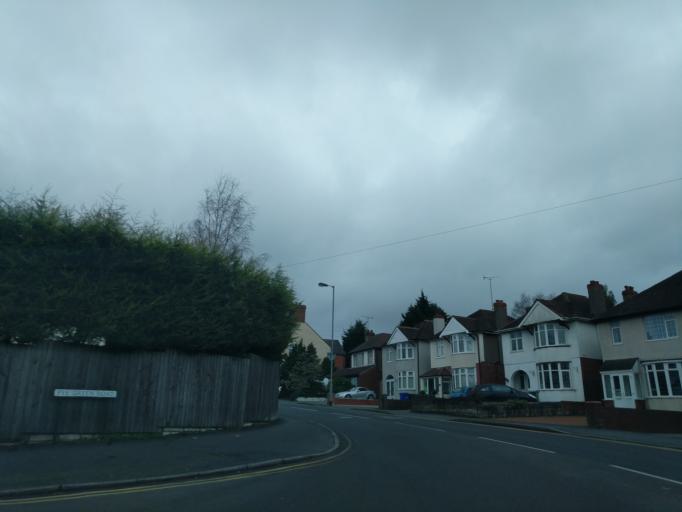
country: GB
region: England
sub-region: Staffordshire
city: Cannock
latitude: 52.6935
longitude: -2.0325
